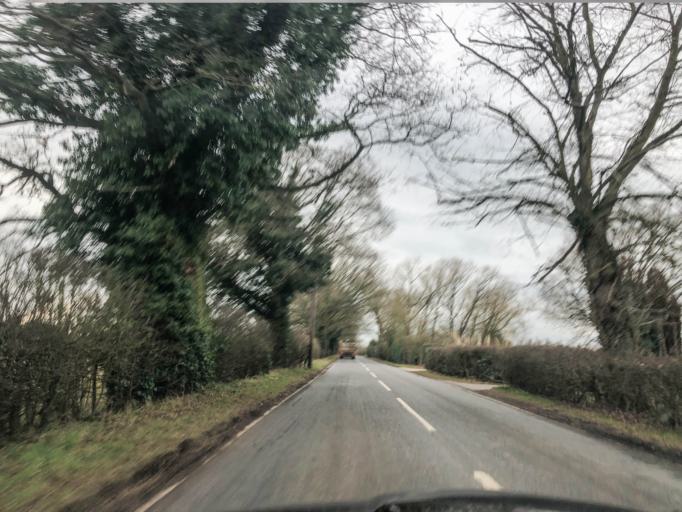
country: GB
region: England
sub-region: Warwickshire
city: Wroxall
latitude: 52.3112
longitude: -1.6783
